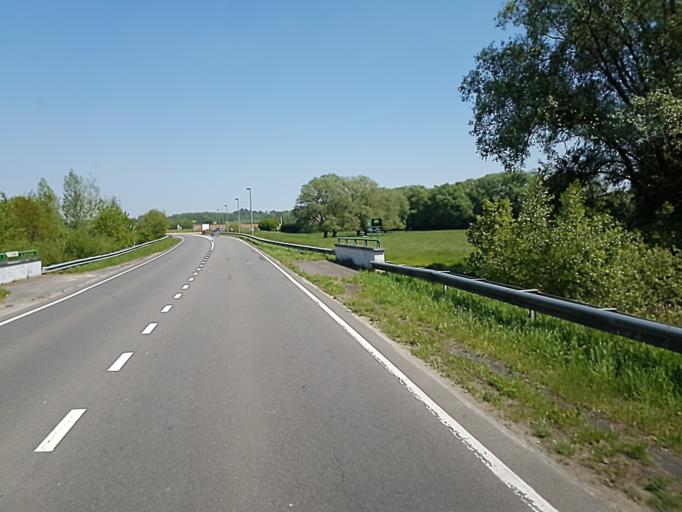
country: BE
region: Wallonia
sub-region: Province du Brabant Wallon
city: Grez-Doiceau
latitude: 50.7458
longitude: 4.6901
